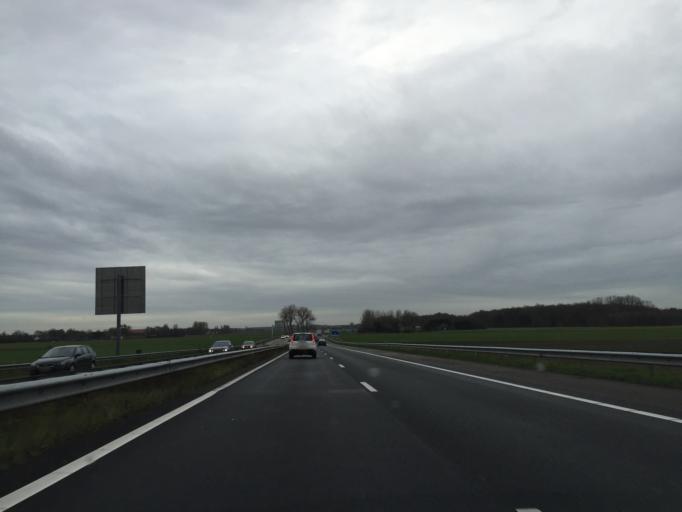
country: NL
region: North Brabant
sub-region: Roosendaal
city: Roosendaal
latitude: 51.5156
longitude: 4.4177
